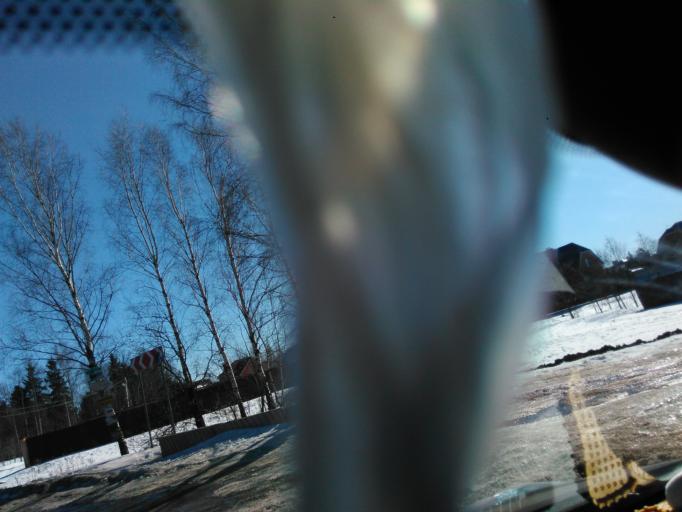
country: RU
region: Moskovskaya
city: Yermolino
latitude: 56.1514
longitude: 37.4831
